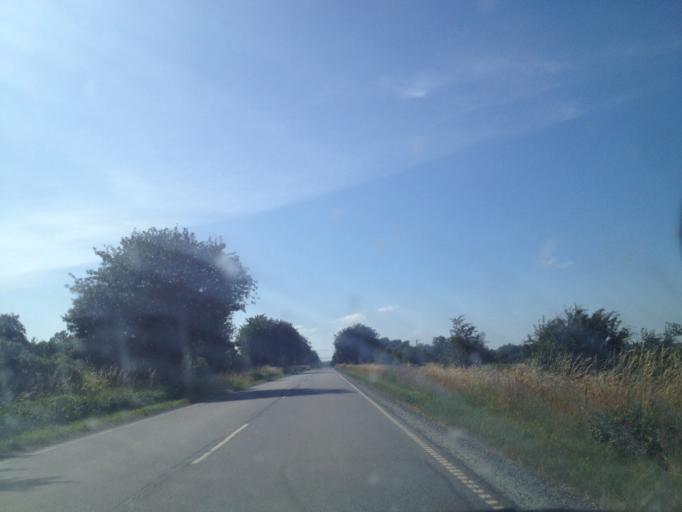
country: DK
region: South Denmark
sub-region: Haderslev Kommune
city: Gram
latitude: 55.2773
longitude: 9.1682
